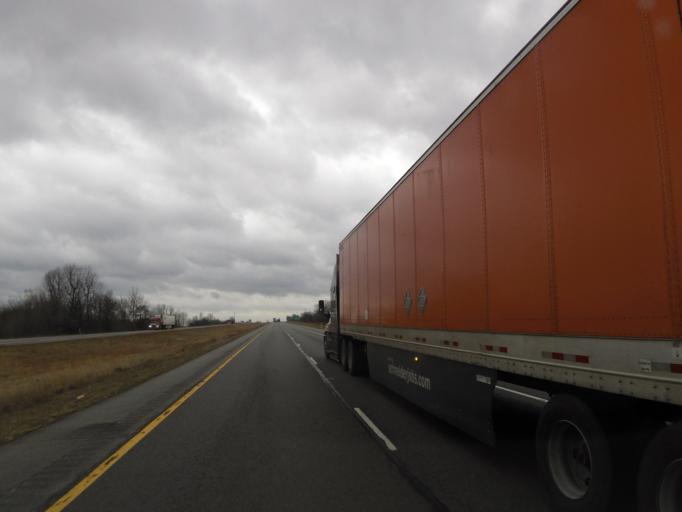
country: US
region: Illinois
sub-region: Massac County
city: Metropolis
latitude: 37.1979
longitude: -88.6896
